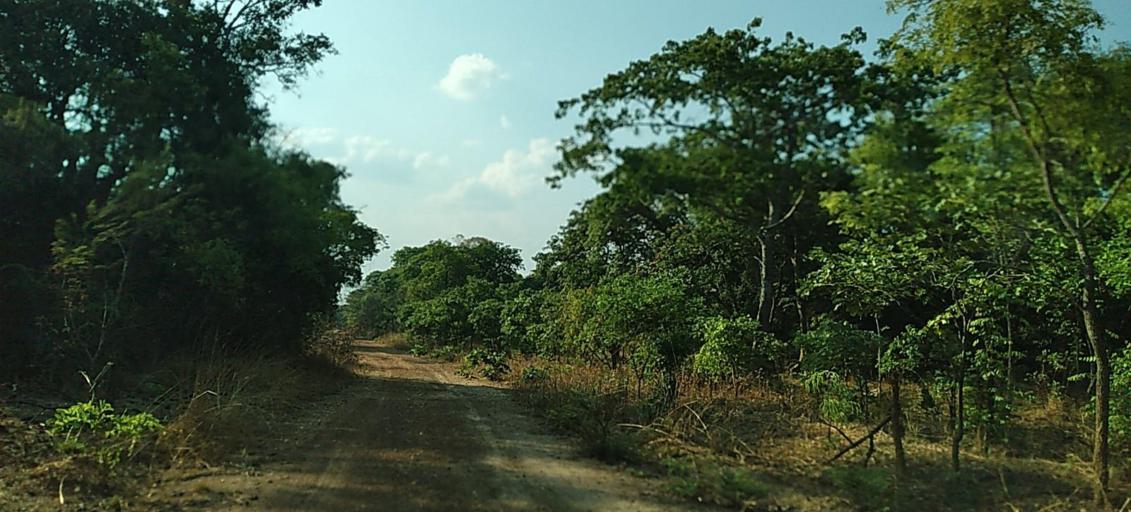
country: ZM
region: Copperbelt
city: Mpongwe
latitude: -13.3915
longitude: 28.0134
